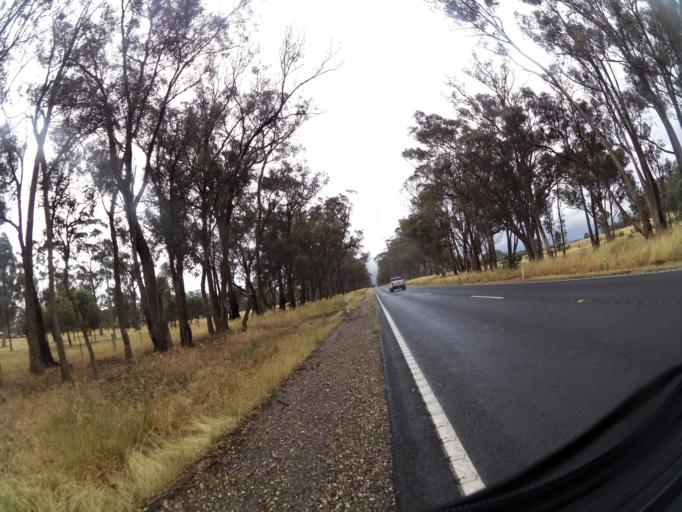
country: AU
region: Victoria
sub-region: Mount Alexander
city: Castlemaine
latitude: -37.0924
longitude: 144.1416
